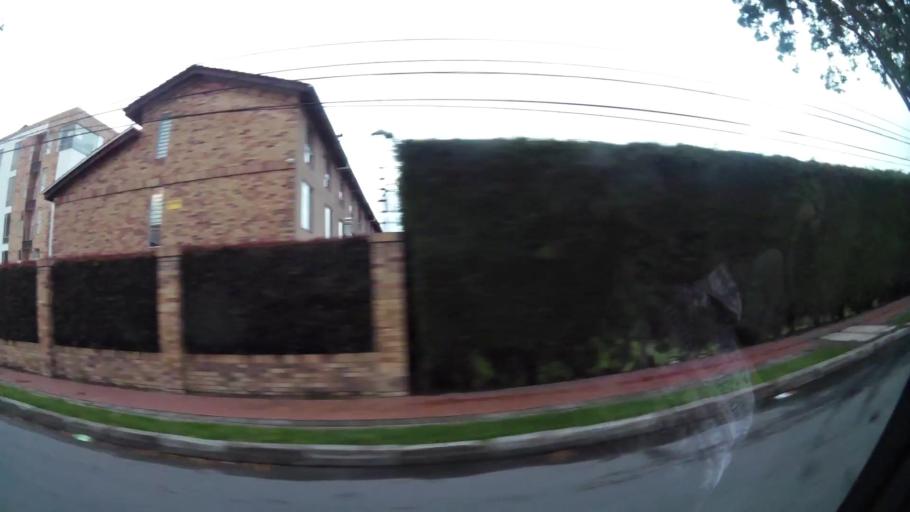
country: CO
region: Cundinamarca
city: Chia
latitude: 4.8488
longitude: -74.0624
